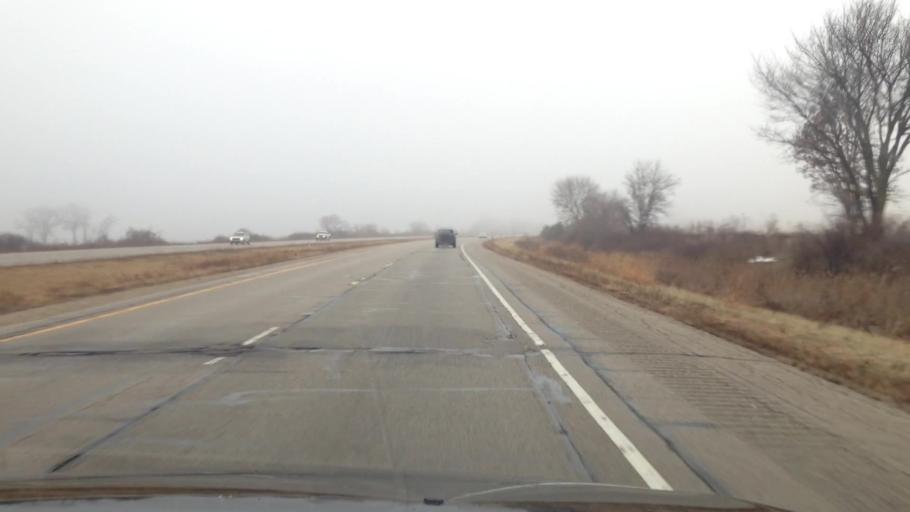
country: US
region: Wisconsin
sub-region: Walworth County
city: Como
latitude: 42.6429
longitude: -88.4962
